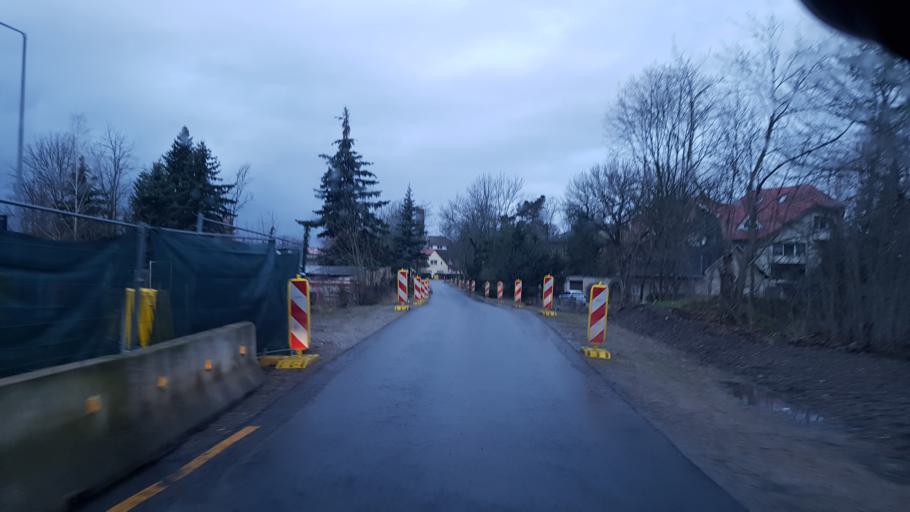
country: DE
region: Brandenburg
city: Herzberg
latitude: 51.6952
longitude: 13.2524
